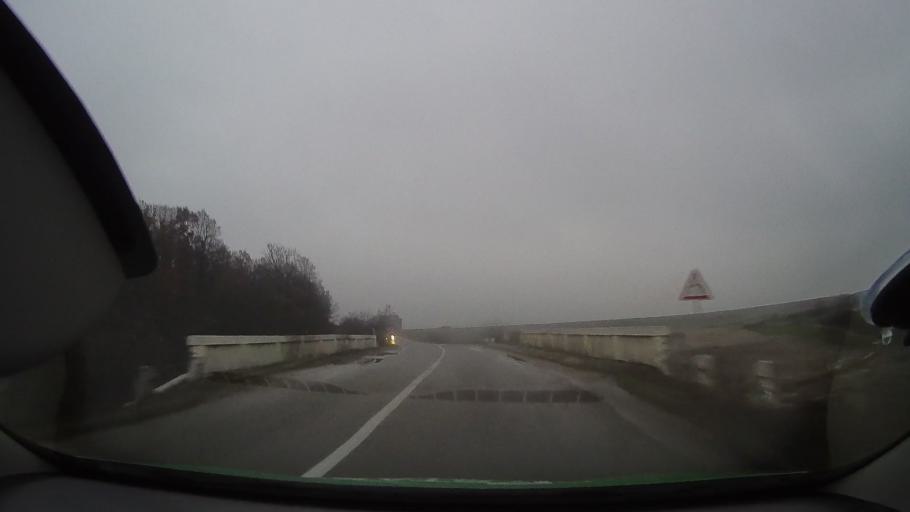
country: RO
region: Bihor
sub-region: Comuna Tinca
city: Gurbediu
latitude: 46.7831
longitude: 21.8676
